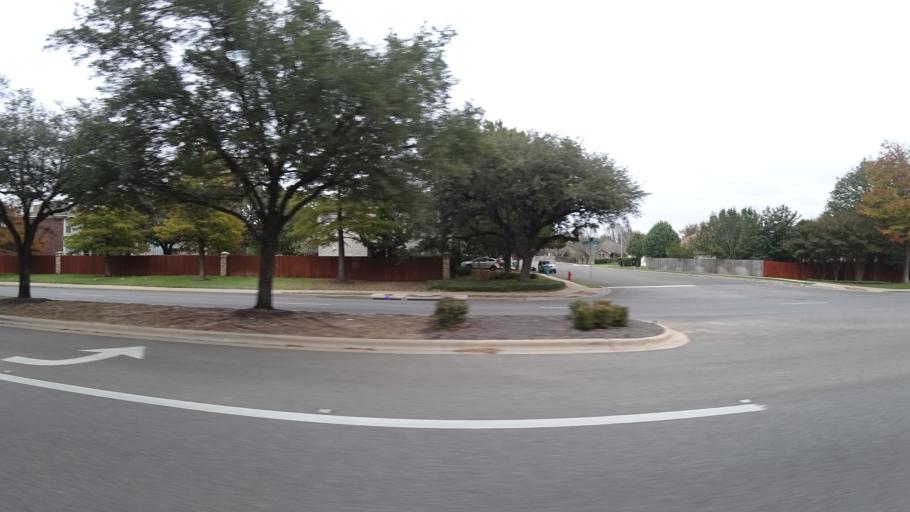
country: US
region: Texas
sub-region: Williamson County
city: Cedar Park
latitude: 30.4910
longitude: -97.8381
